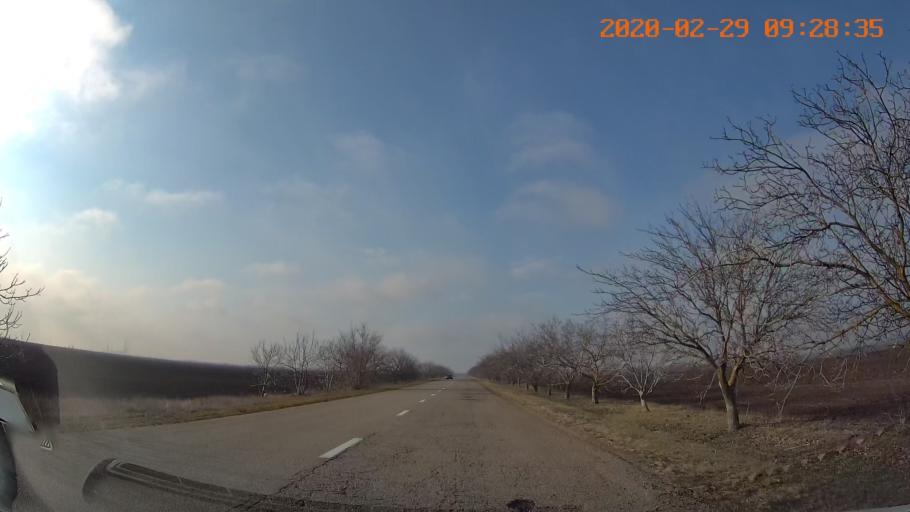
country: UA
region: Odessa
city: Lymanske
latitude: 46.6873
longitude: 29.9282
